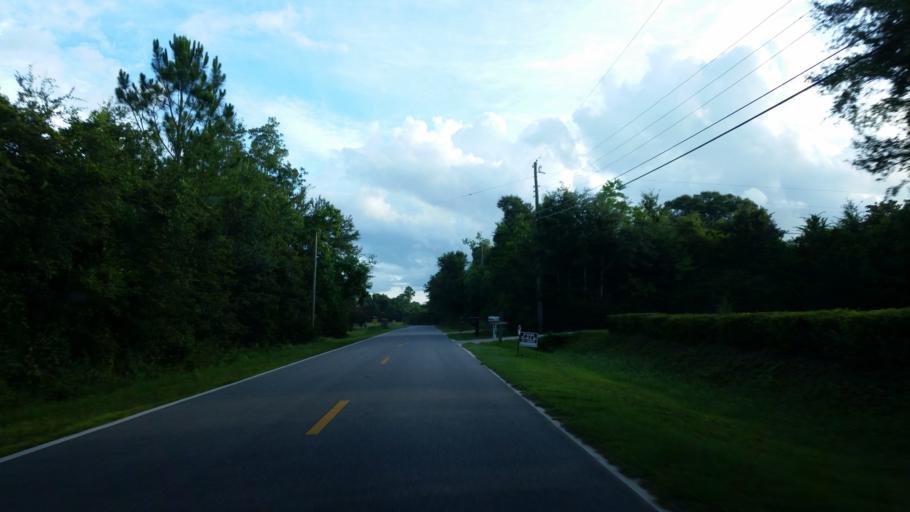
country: US
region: Florida
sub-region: Escambia County
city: Ensley
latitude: 30.5265
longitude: -87.3301
